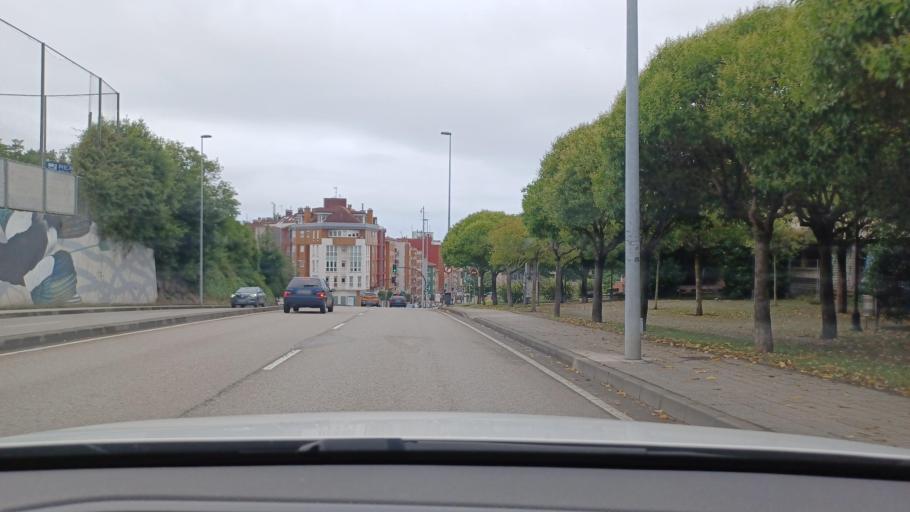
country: ES
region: Asturias
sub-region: Province of Asturias
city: Gijon
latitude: 43.5295
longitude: -5.6548
